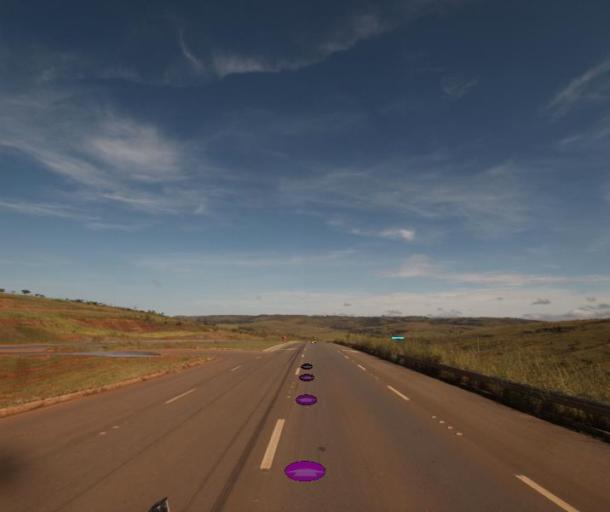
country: BR
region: Federal District
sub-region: Brasilia
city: Brasilia
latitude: -15.7553
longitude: -48.3374
